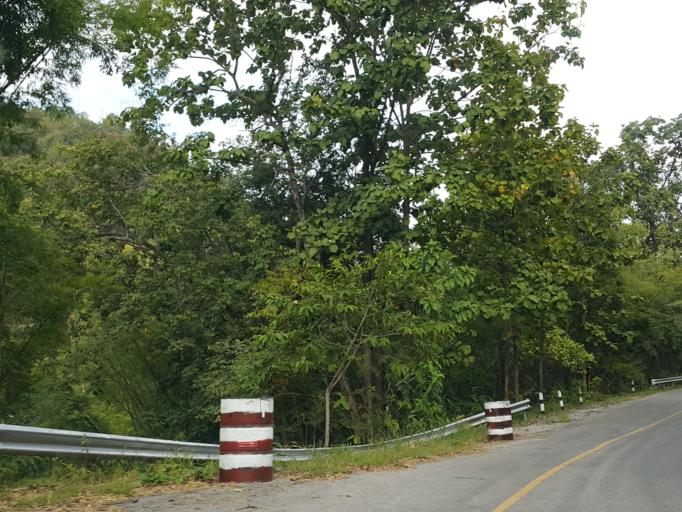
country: TH
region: Lampang
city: Chae Hom
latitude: 18.6516
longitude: 99.5144
